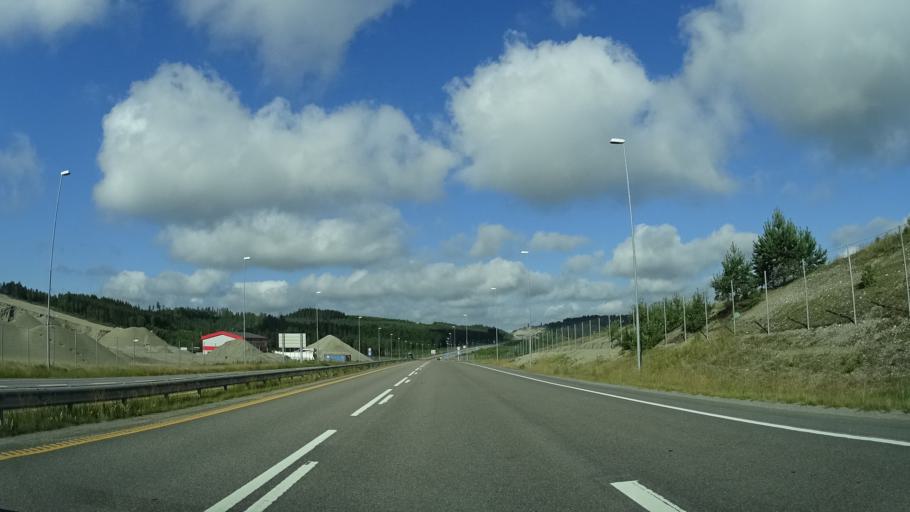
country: NO
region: Ostfold
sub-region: Eidsberg
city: Mysen
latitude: 59.5766
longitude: 11.3205
